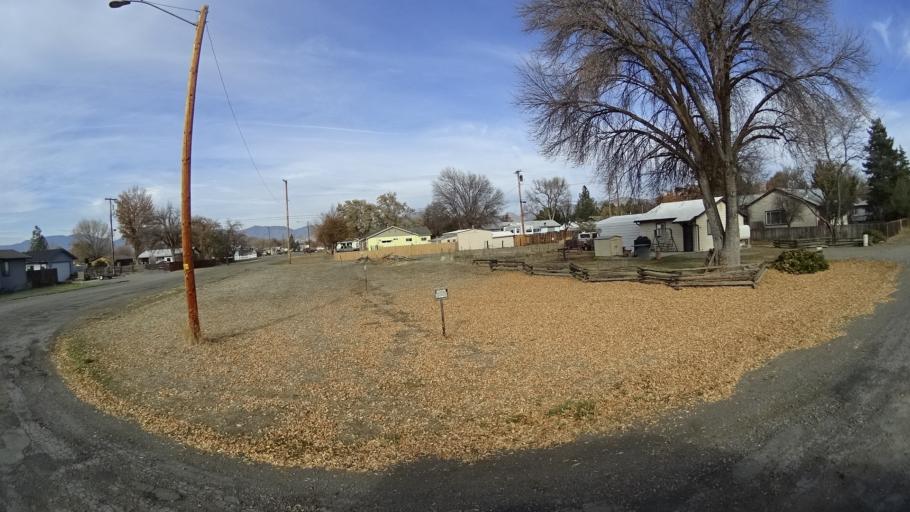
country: US
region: California
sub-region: Siskiyou County
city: Montague
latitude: 41.7244
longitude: -122.5216
